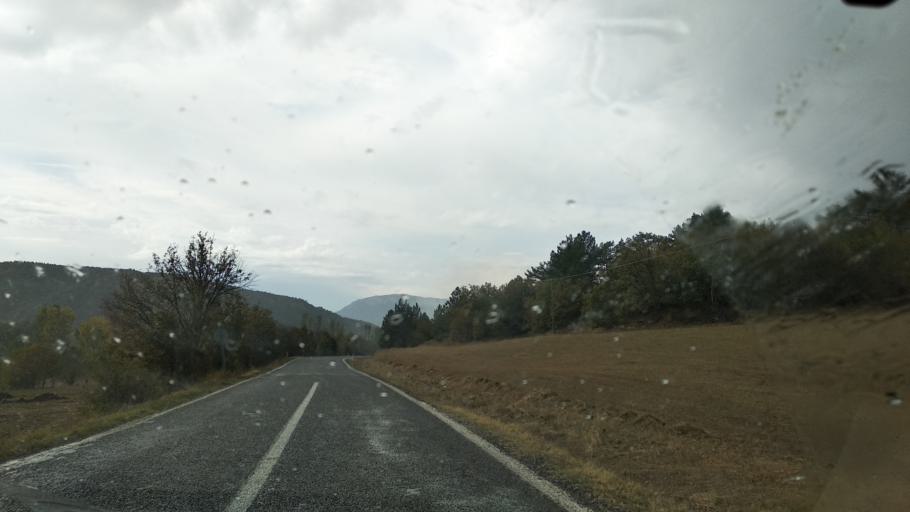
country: TR
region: Ankara
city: Nallihan
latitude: 40.3247
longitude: 31.4018
